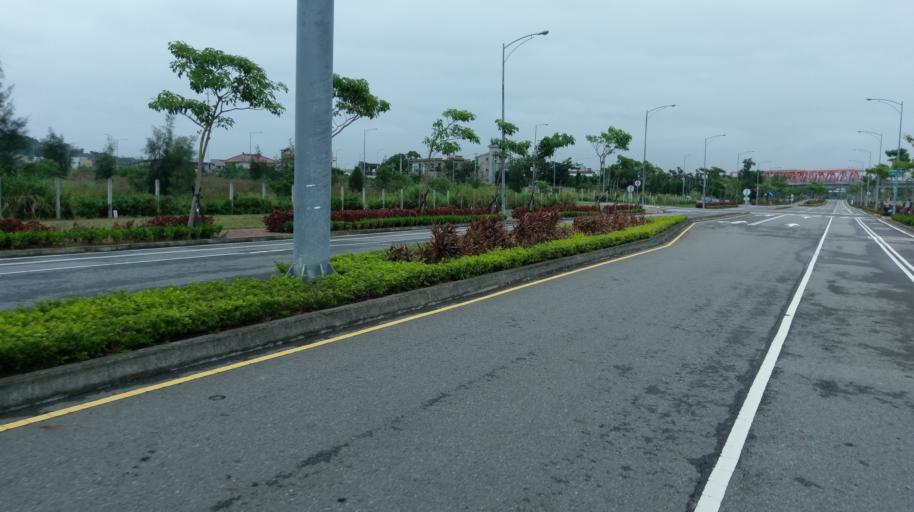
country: TW
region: Taiwan
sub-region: Miaoli
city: Miaoli
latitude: 24.6092
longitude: 120.8234
